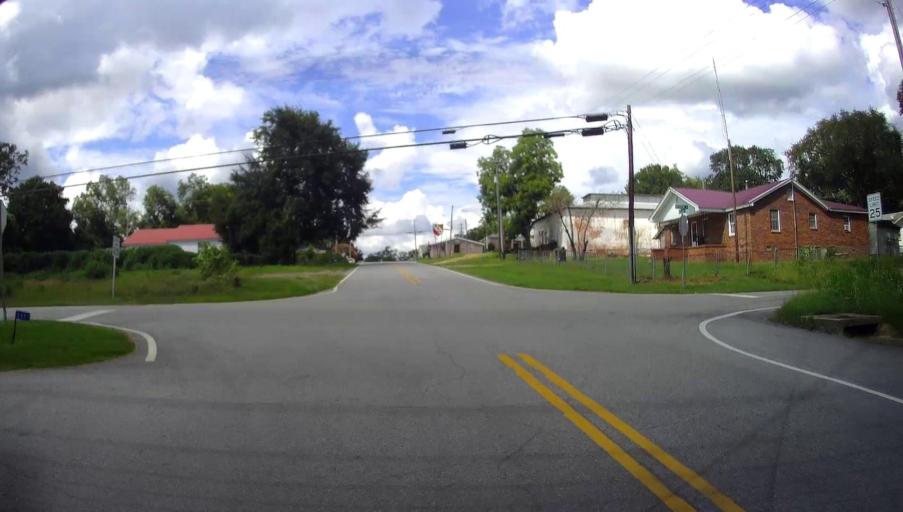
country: US
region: Georgia
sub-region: Chattahoochee County
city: Cusseta
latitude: 32.3054
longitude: -84.7774
